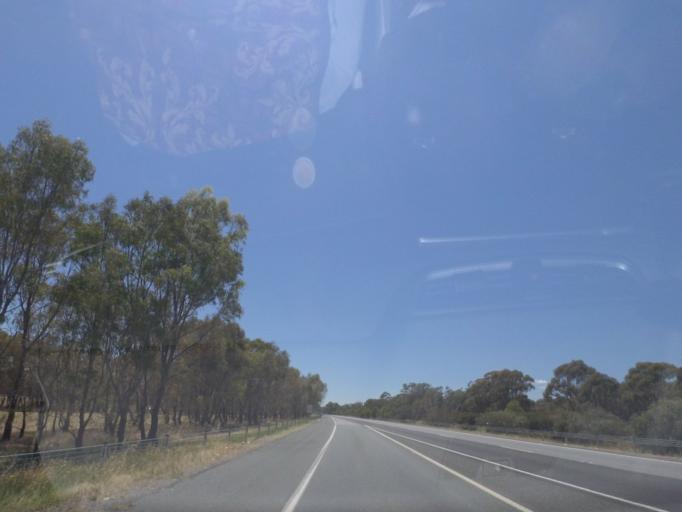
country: AU
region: Victoria
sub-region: Benalla
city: Benalla
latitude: -36.7129
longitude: 145.6385
